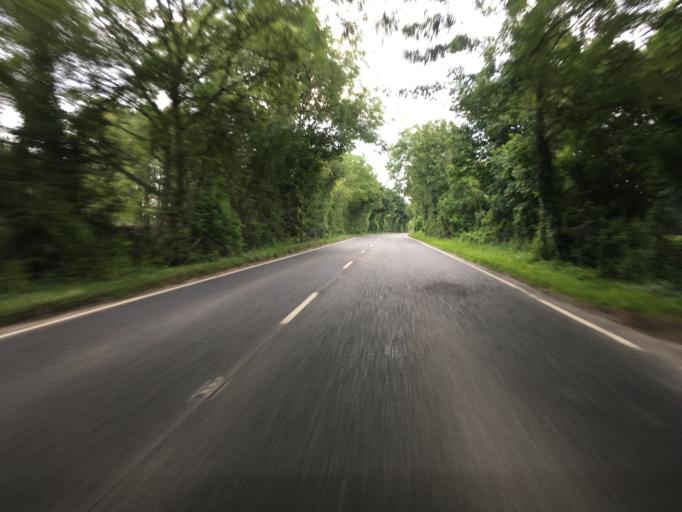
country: GB
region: England
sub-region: North Somerset
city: Long Ashton
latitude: 51.4436
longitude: -2.6766
